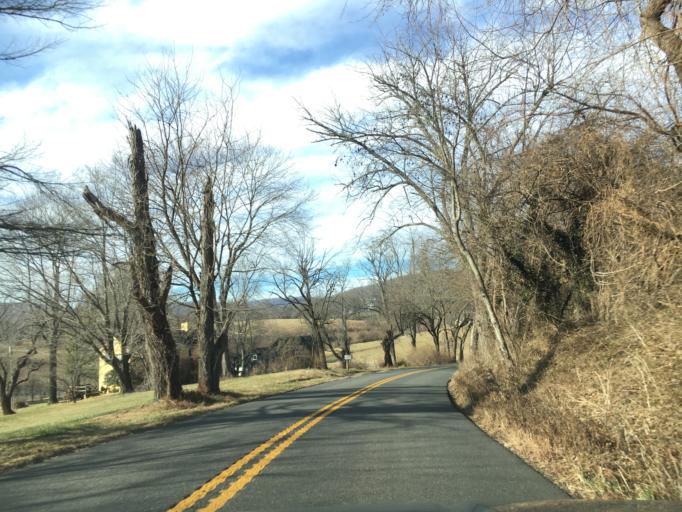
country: US
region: Virginia
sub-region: Warren County
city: Apple Mountain Lake
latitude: 38.8779
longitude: -78.0029
